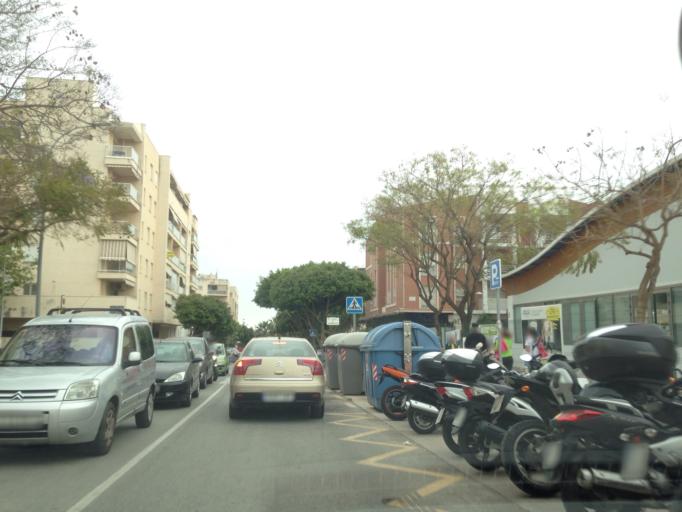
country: ES
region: Andalusia
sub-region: Provincia de Malaga
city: Malaga
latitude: 36.7228
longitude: -4.4800
